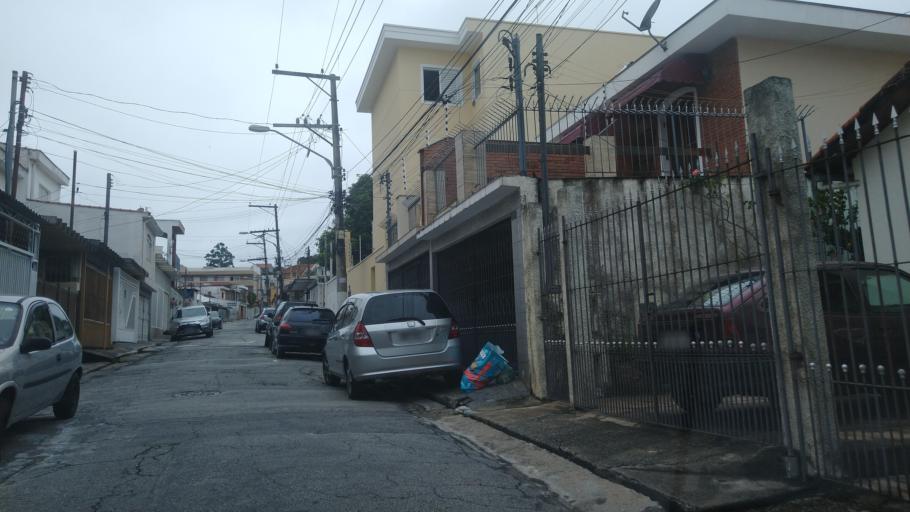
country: BR
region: Sao Paulo
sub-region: Sao Paulo
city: Sao Paulo
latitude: -23.4941
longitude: -46.6064
